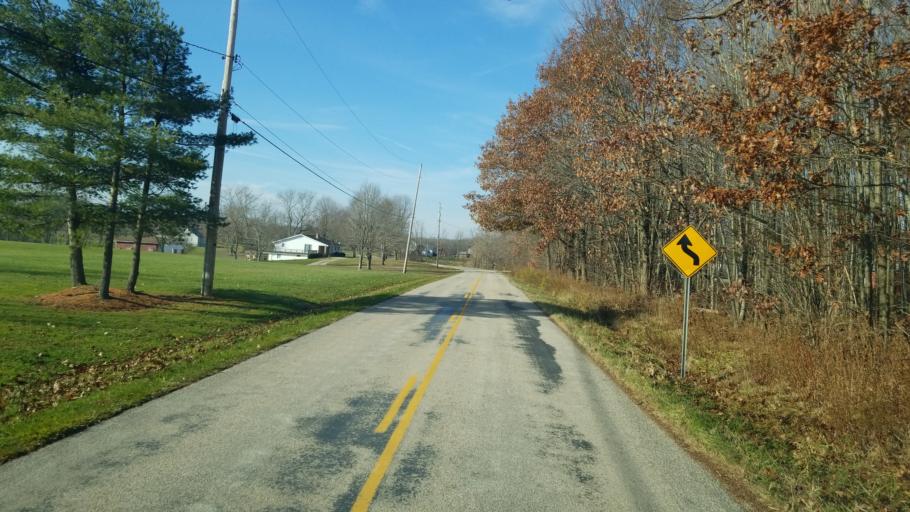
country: US
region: Ohio
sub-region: Ashtabula County
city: North Kingsville
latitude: 41.8245
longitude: -80.6943
